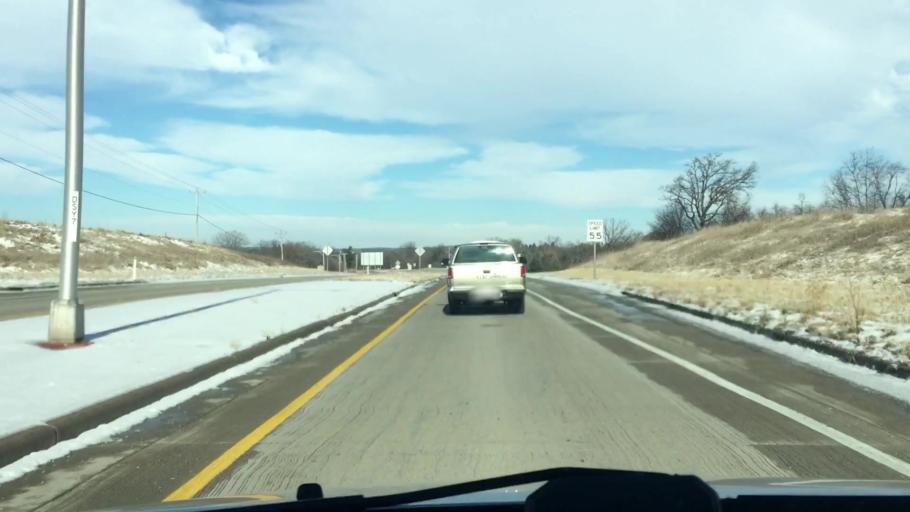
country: US
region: Wisconsin
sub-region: Waukesha County
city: North Prairie
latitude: 42.9352
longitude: -88.3463
